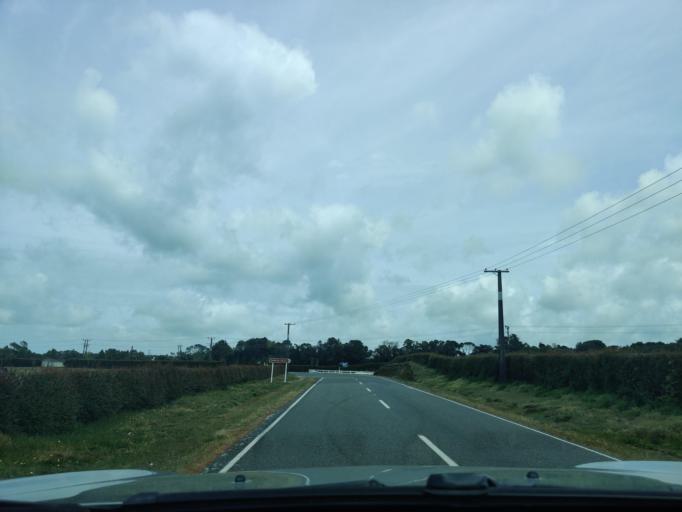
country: NZ
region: Taranaki
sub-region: South Taranaki District
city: Eltham
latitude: -39.3852
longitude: 174.1466
